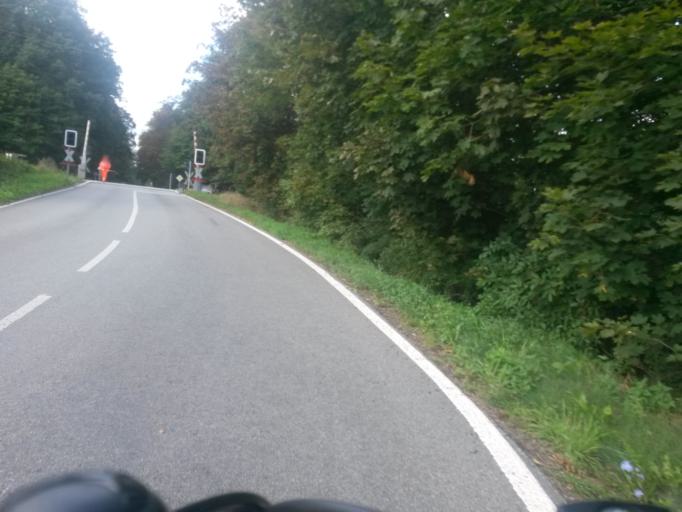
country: DE
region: Brandenburg
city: Angermunde
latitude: 53.0532
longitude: 13.9421
